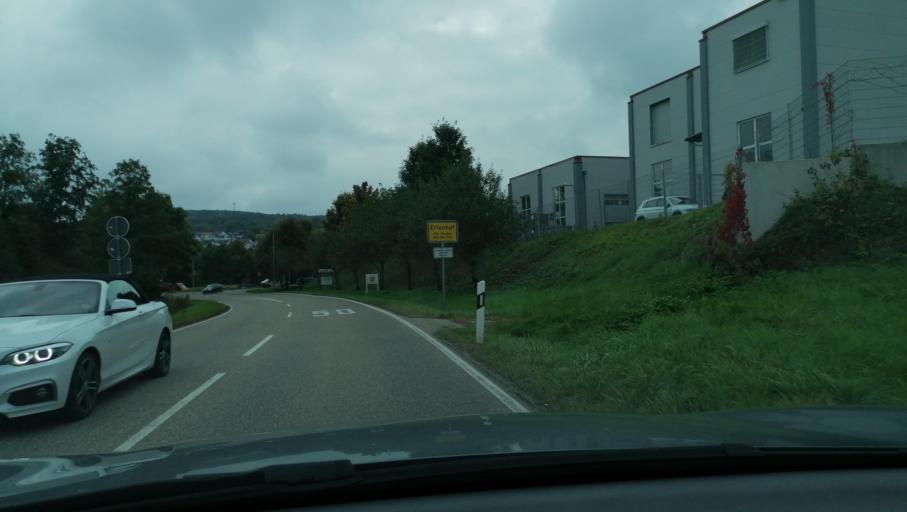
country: DE
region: Baden-Wuerttemberg
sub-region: Regierungsbezirk Stuttgart
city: Winterbach
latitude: 48.8483
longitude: 9.4493
